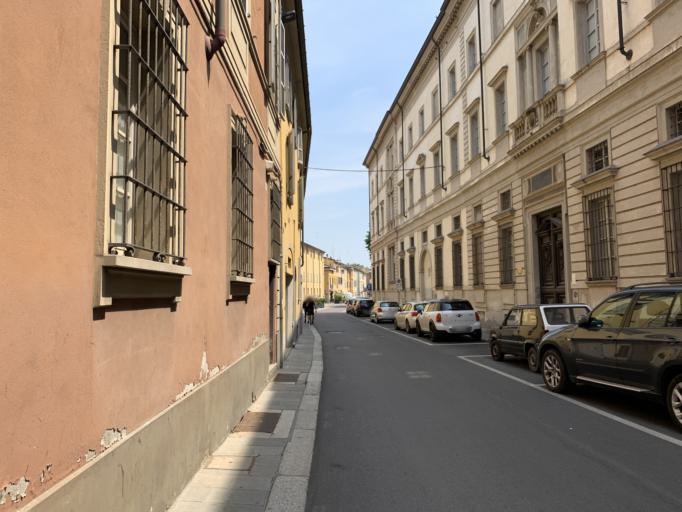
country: IT
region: Emilia-Romagna
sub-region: Provincia di Piacenza
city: Piacenza
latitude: 45.0482
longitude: 9.7006
